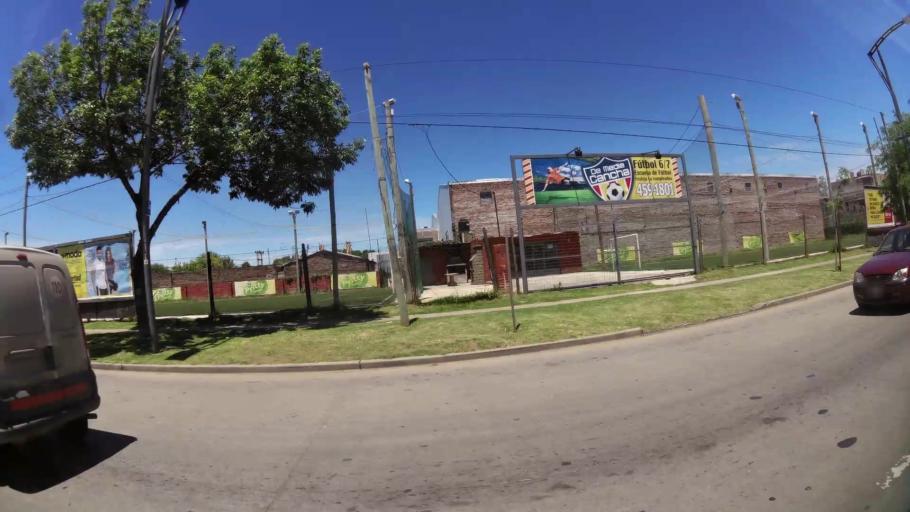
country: AR
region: Santa Fe
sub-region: Departamento de Rosario
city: Rosario
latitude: -32.9485
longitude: -60.7092
